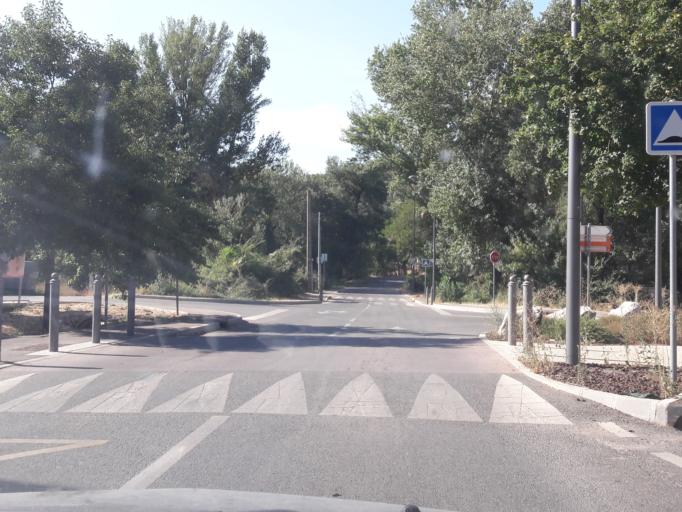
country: FR
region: Provence-Alpes-Cote d'Azur
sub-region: Departement des Bouches-du-Rhone
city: Gardanne
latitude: 43.4694
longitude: 5.4510
